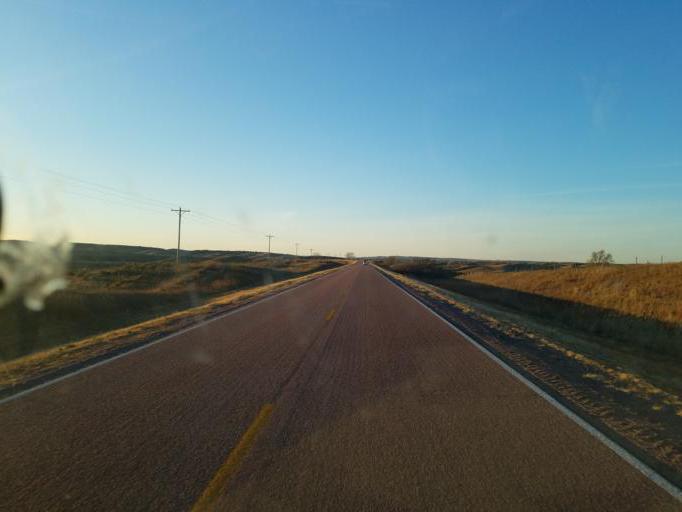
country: US
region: South Dakota
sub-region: Bon Homme County
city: Springfield
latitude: 42.7385
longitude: -97.9090
